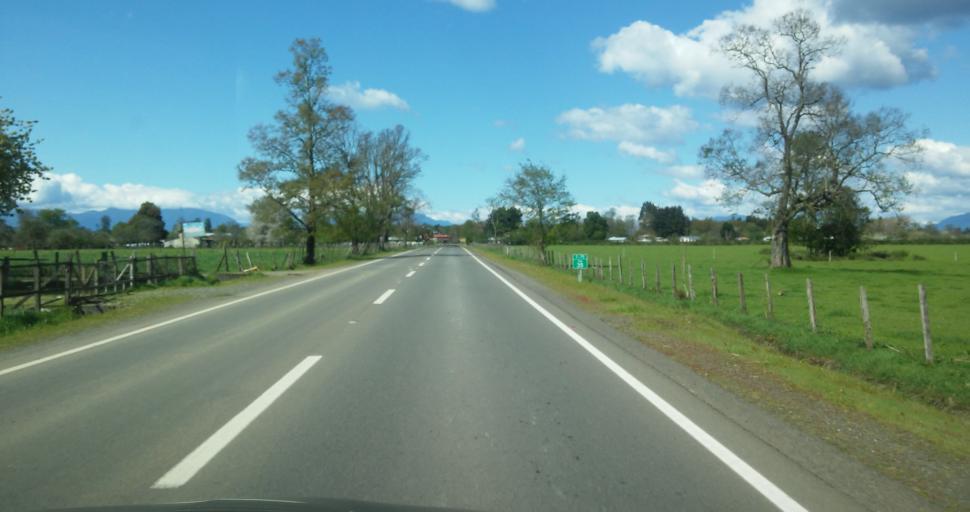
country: CL
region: Los Rios
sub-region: Provincia del Ranco
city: Rio Bueno
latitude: -40.2397
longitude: -72.5989
